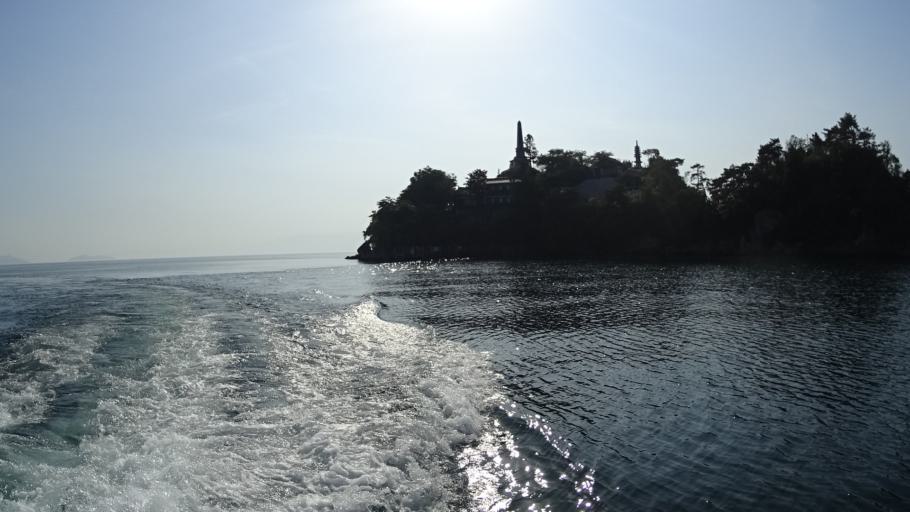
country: JP
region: Shiga Prefecture
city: Hikone
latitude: 35.2962
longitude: 136.1794
